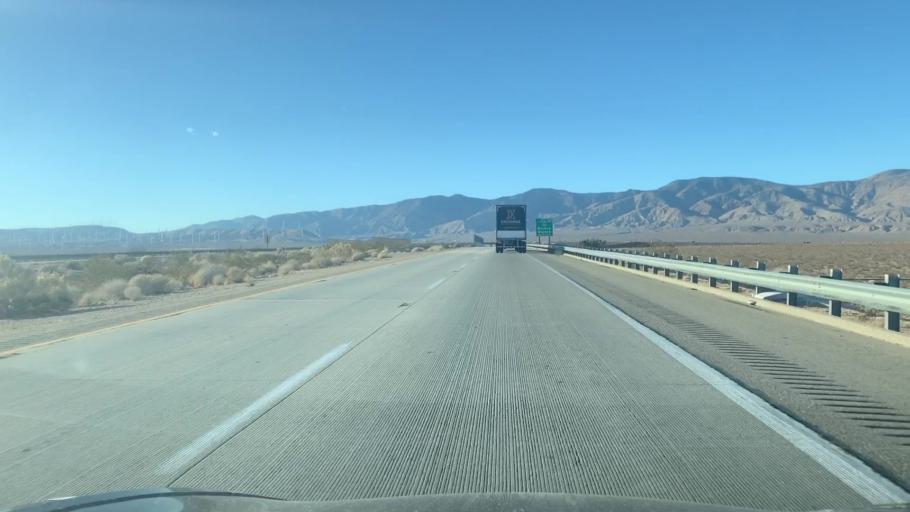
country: US
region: California
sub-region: Kern County
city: Mojave
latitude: 35.0929
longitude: -118.1310
